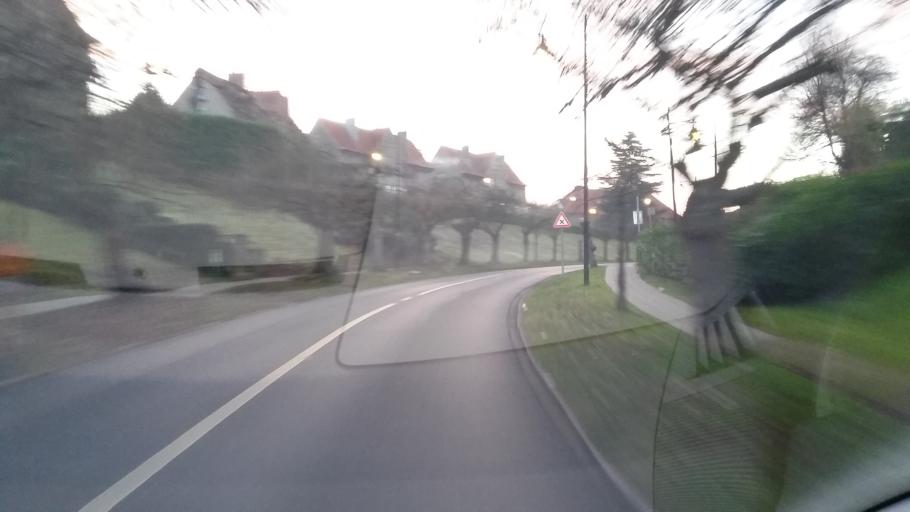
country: BE
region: Flanders
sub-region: Provincie Vlaams-Brabant
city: Hoeilaart
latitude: 50.8076
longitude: 4.4240
